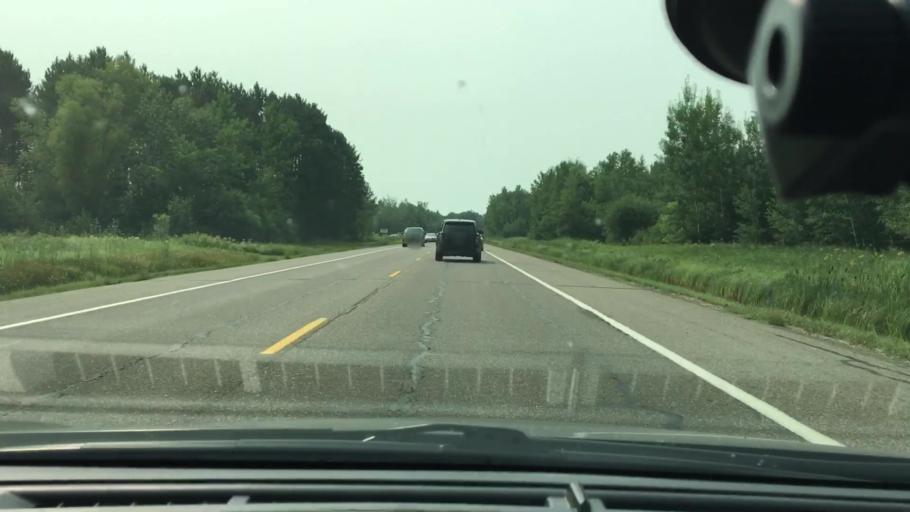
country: US
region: Minnesota
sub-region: Crow Wing County
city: Brainerd
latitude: 46.3903
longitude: -94.2233
